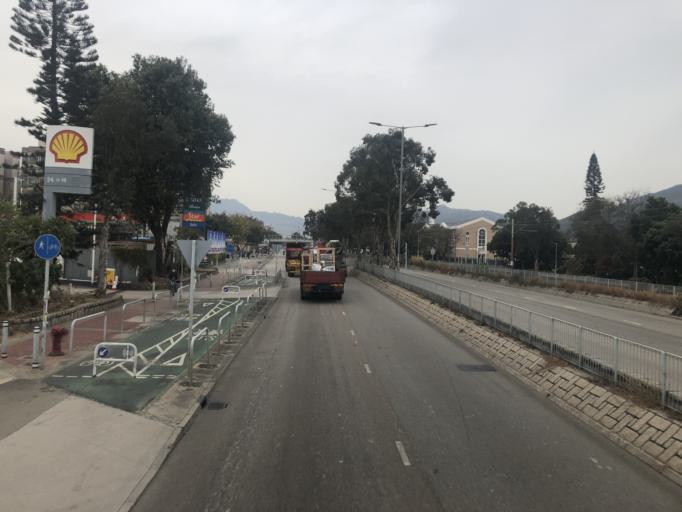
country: HK
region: Yuen Long
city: Yuen Long Kau Hui
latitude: 22.4318
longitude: 113.9952
